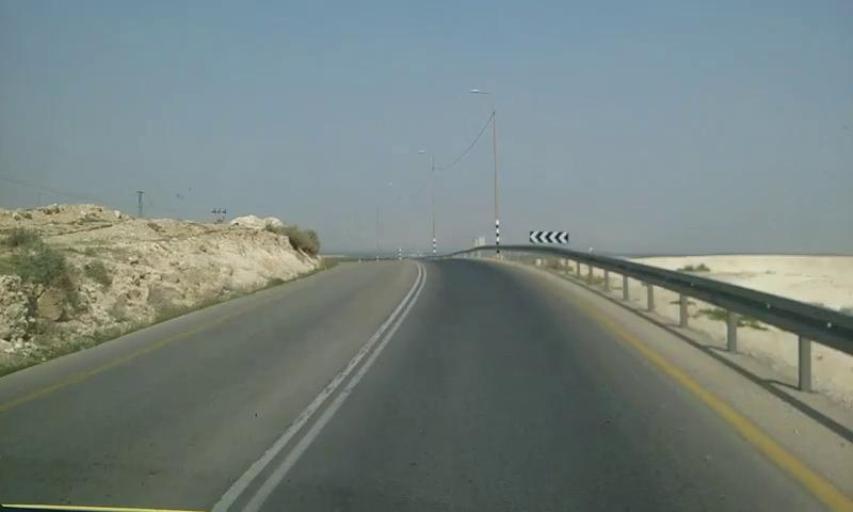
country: PS
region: West Bank
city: Al `Awja
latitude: 31.9716
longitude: 35.4704
